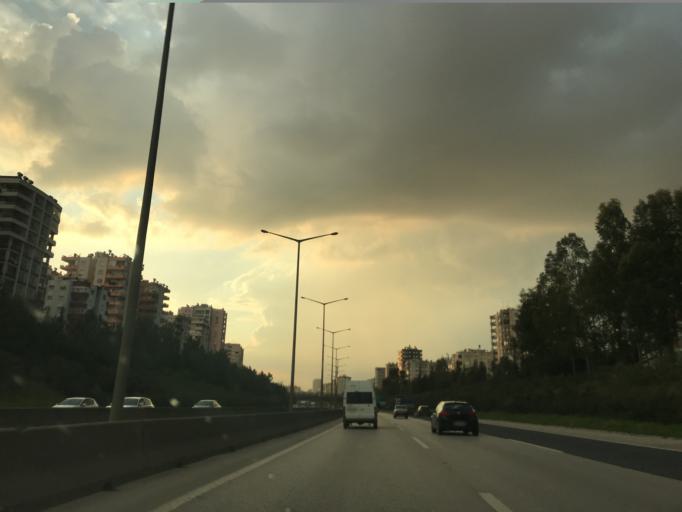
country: TR
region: Adana
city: Adana
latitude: 37.0324
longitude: 35.3045
